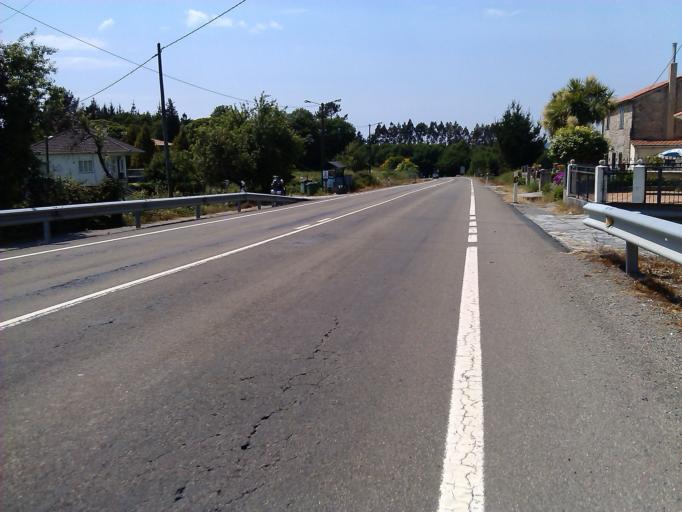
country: ES
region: Galicia
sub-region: Provincia de Lugo
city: Monterroso
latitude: 42.8748
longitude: -7.8504
